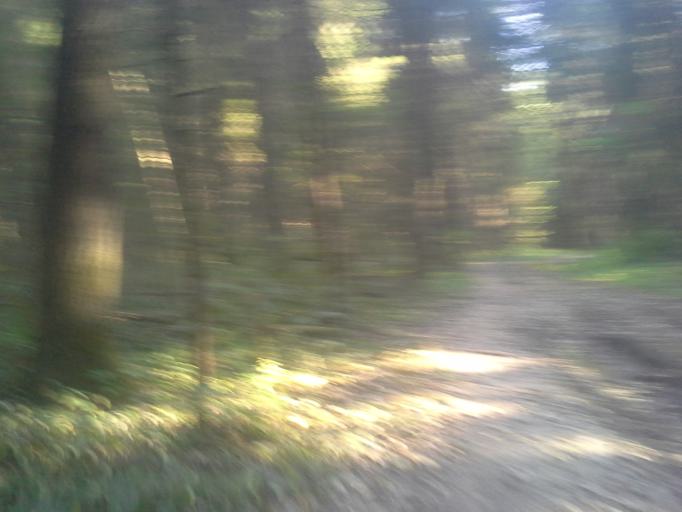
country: RU
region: Moskovskaya
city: Selyatino
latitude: 55.4631
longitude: 36.9893
